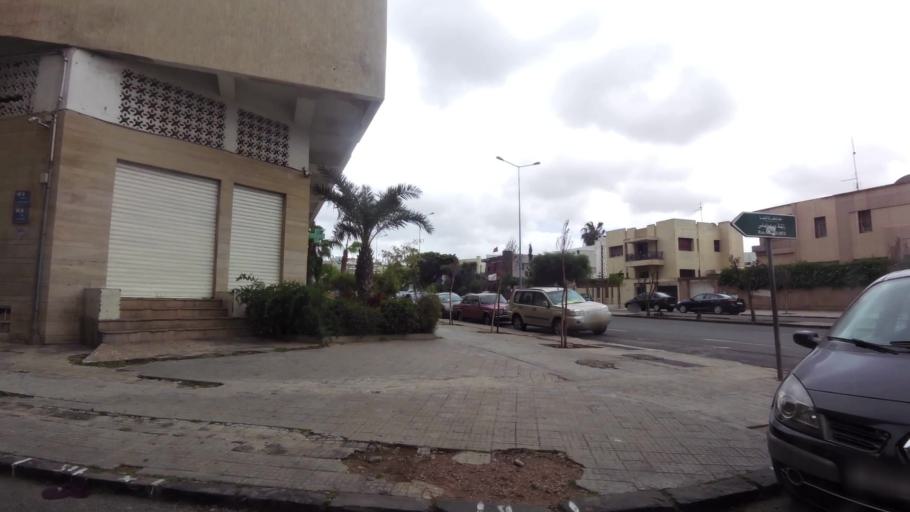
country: MA
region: Grand Casablanca
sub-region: Casablanca
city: Casablanca
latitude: 33.5959
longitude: -7.6470
